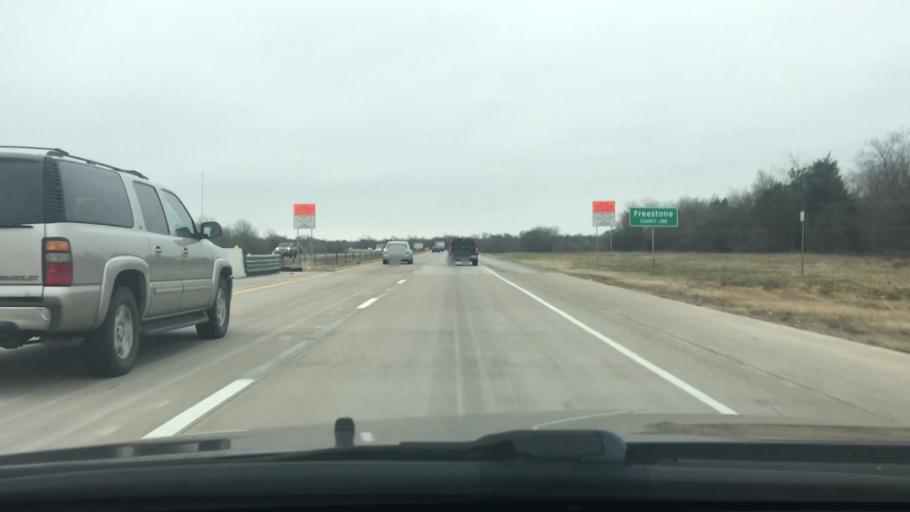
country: US
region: Texas
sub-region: Freestone County
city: Wortham
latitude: 31.8737
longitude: -96.3397
